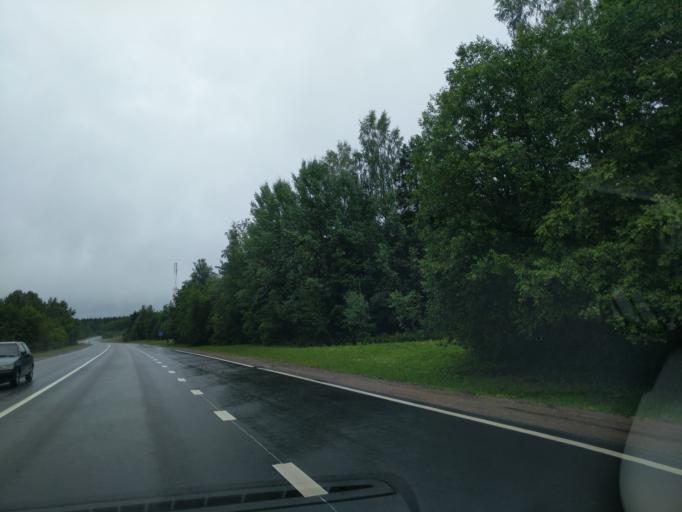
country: BY
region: Minsk
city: Syomkava
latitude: 54.1623
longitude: 27.5018
